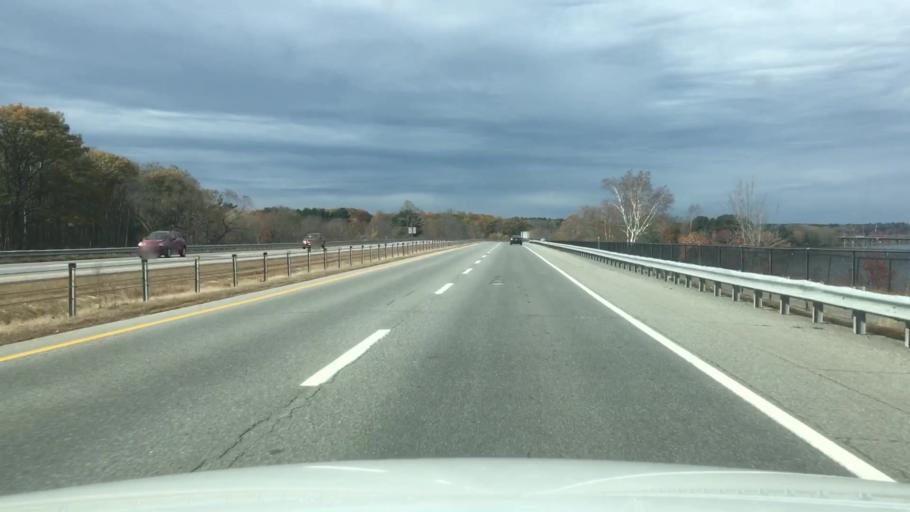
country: US
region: Maine
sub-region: Cumberland County
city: Brunswick
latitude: 43.9104
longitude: -69.9323
